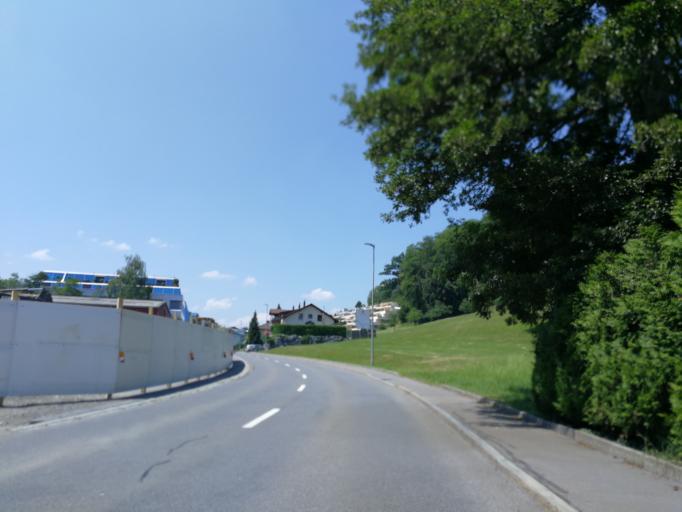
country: CH
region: Schwyz
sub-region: Bezirk Hoefe
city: Wollerau
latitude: 47.1904
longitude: 8.7107
